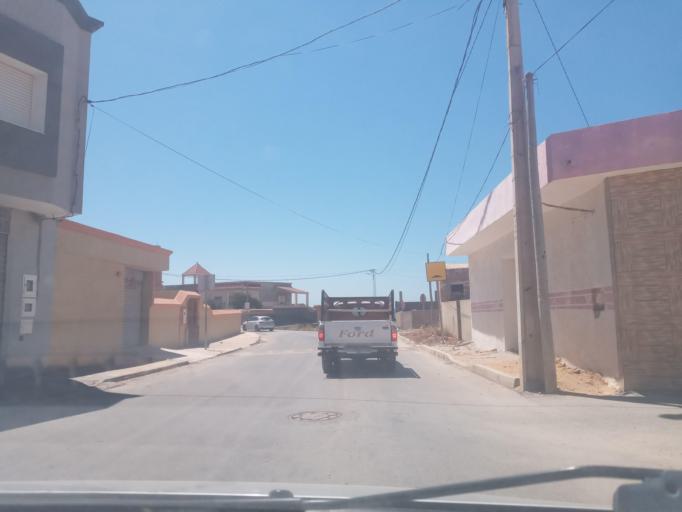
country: TN
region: Nabul
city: El Haouaria
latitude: 37.0543
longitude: 10.9920
